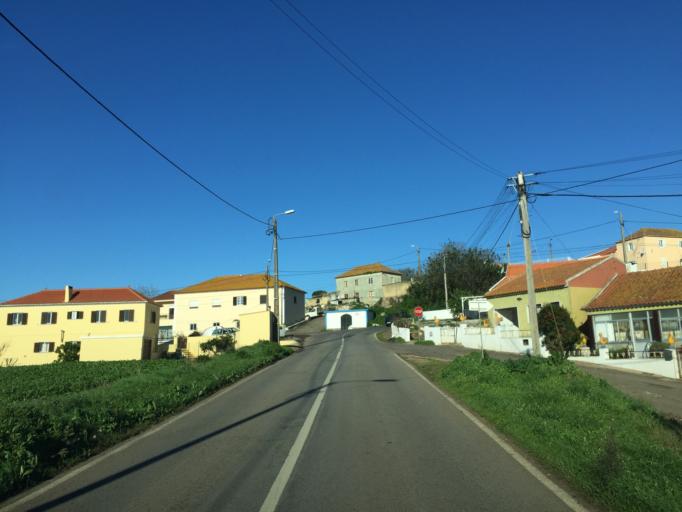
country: PT
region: Lisbon
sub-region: Sintra
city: Almargem
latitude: 38.8671
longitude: -9.2843
